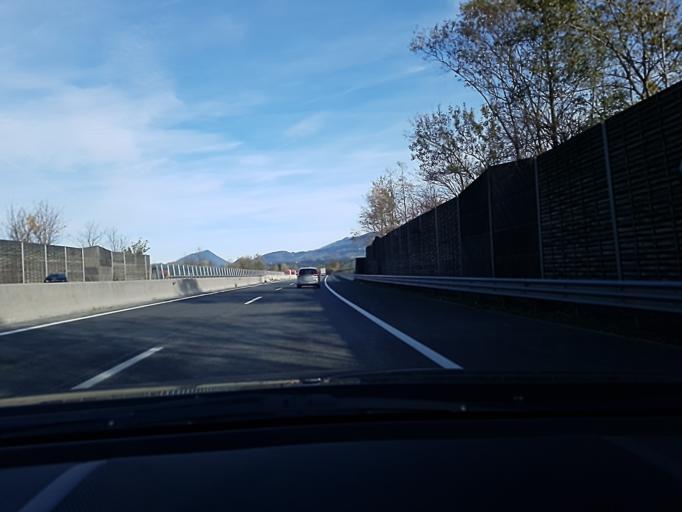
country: AT
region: Salzburg
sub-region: Politischer Bezirk Hallein
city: Kuchl
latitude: 47.6327
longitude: 13.1322
